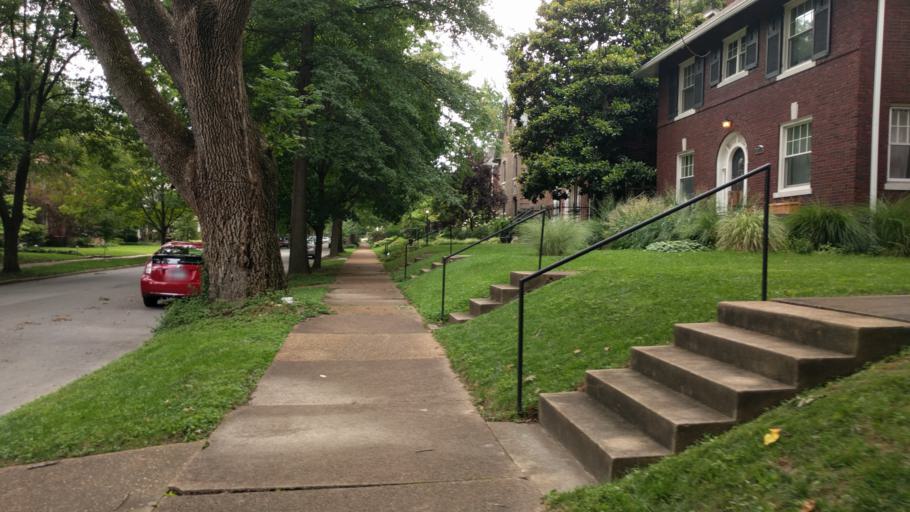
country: US
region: Missouri
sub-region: Saint Louis County
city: University City
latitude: 38.6521
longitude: -90.3122
